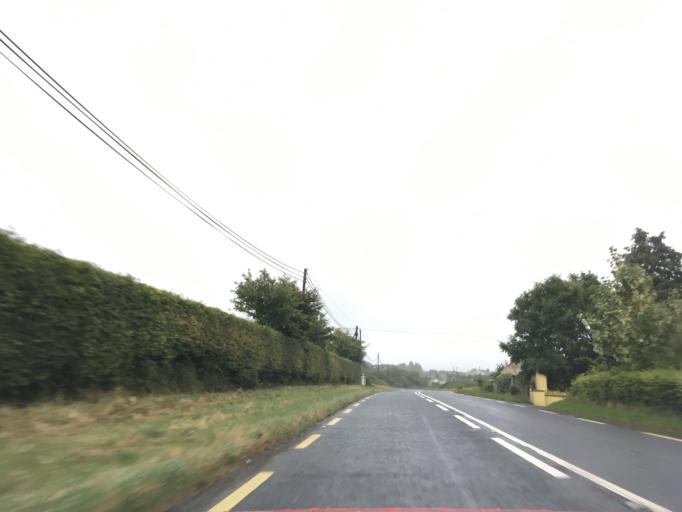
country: IE
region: Munster
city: Tipperary
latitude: 52.4812
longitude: -8.1015
